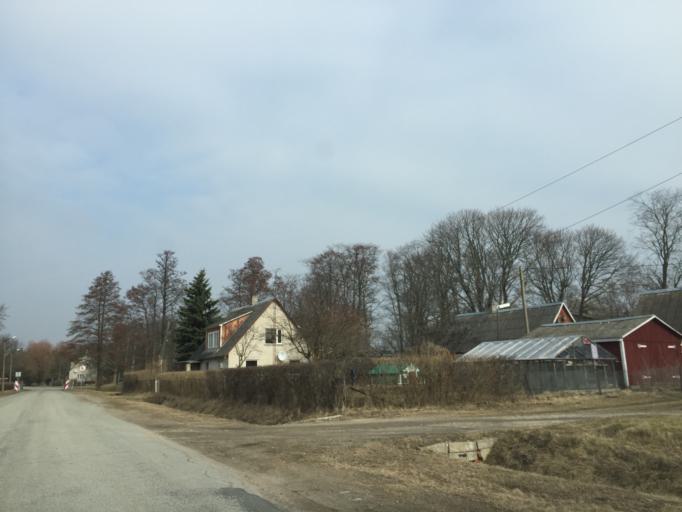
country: LV
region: Salacgrivas
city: Ainazi
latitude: 57.9194
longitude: 24.3873
